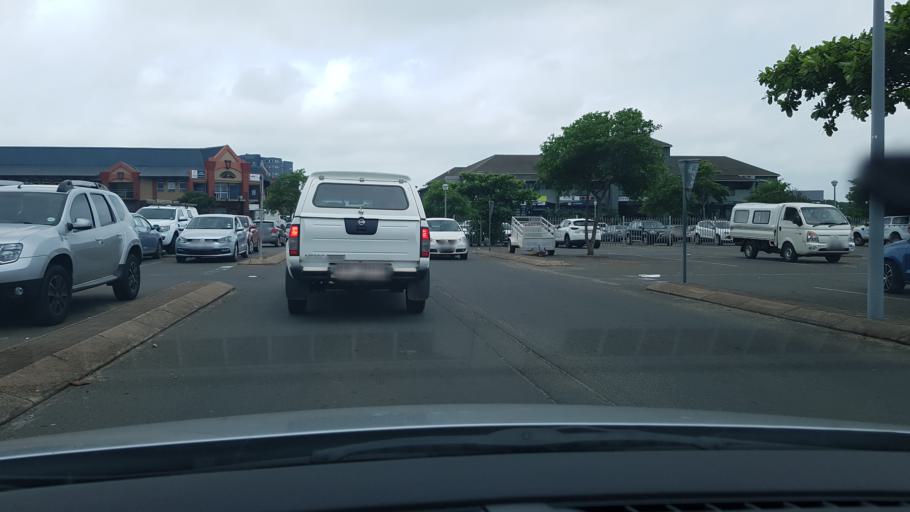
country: ZA
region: KwaZulu-Natal
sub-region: uThungulu District Municipality
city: Richards Bay
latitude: -28.7539
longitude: 32.0529
